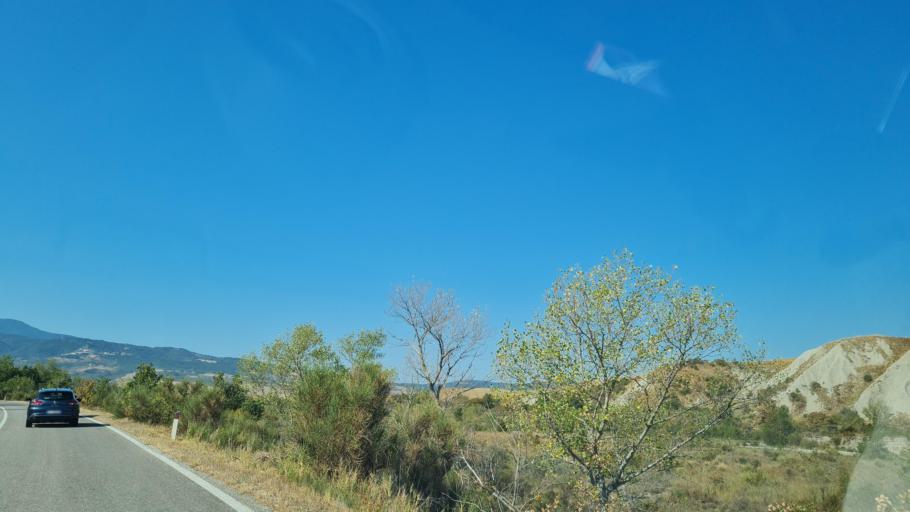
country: IT
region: Tuscany
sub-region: Provincia di Siena
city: Pienza
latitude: 42.9907
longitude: 11.7182
